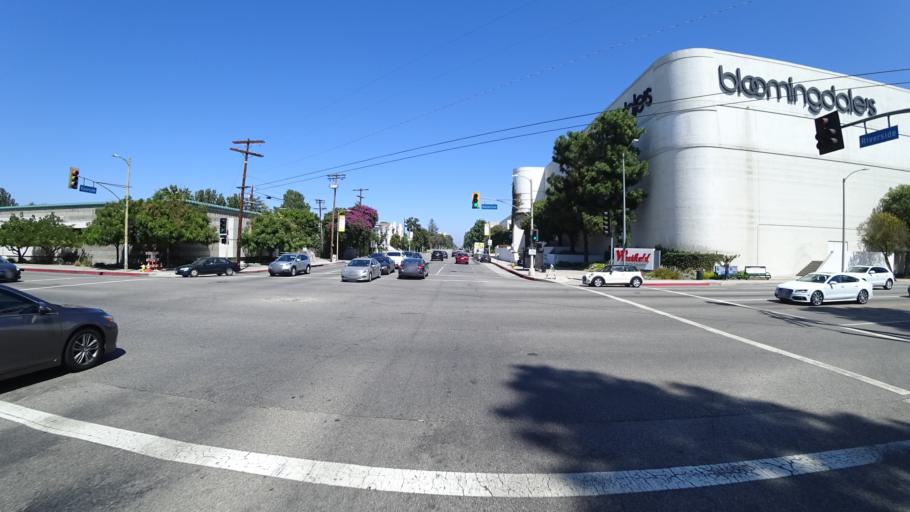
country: US
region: California
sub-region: Los Angeles County
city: Sherman Oaks
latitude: 34.1576
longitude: -118.4402
